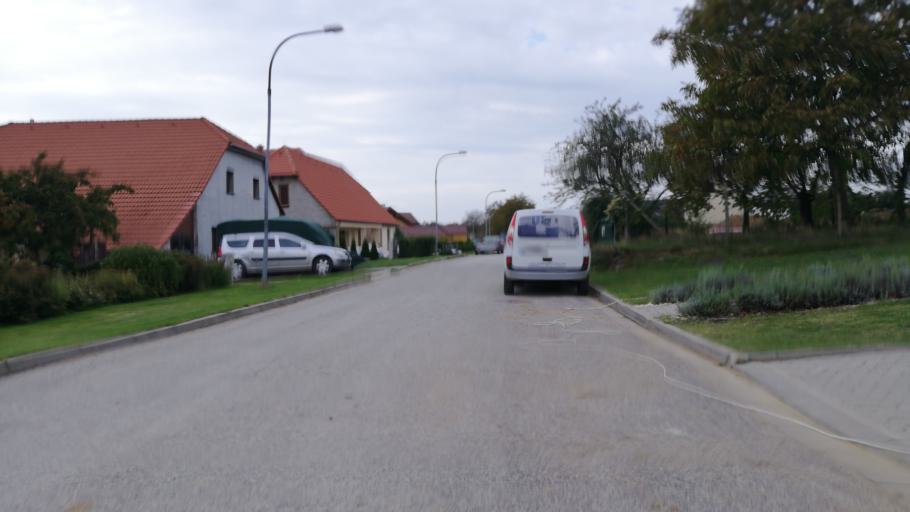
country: SK
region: Trnavsky
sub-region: Okres Skalica
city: Skalica
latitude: 48.8164
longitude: 17.2429
